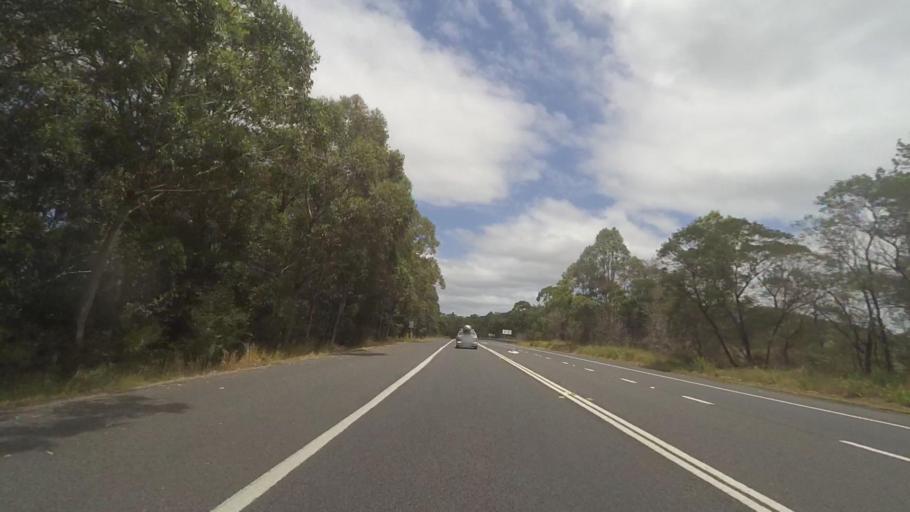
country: AU
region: New South Wales
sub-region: Shoalhaven Shire
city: Milton
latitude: -35.2314
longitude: 150.4333
